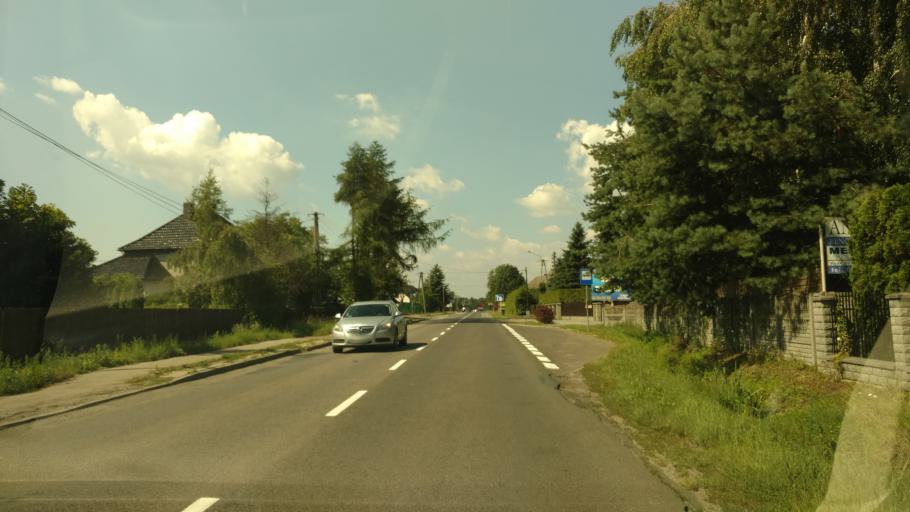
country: PL
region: Silesian Voivodeship
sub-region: Powiat pszczynski
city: Pszczyna
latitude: 49.9939
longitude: 18.9655
